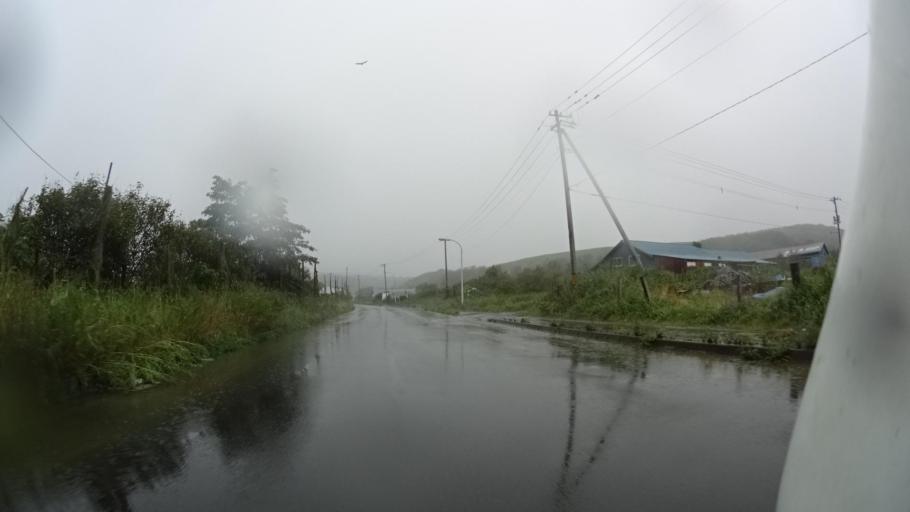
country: JP
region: Hokkaido
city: Nemuro
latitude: 43.2824
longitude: 145.5651
